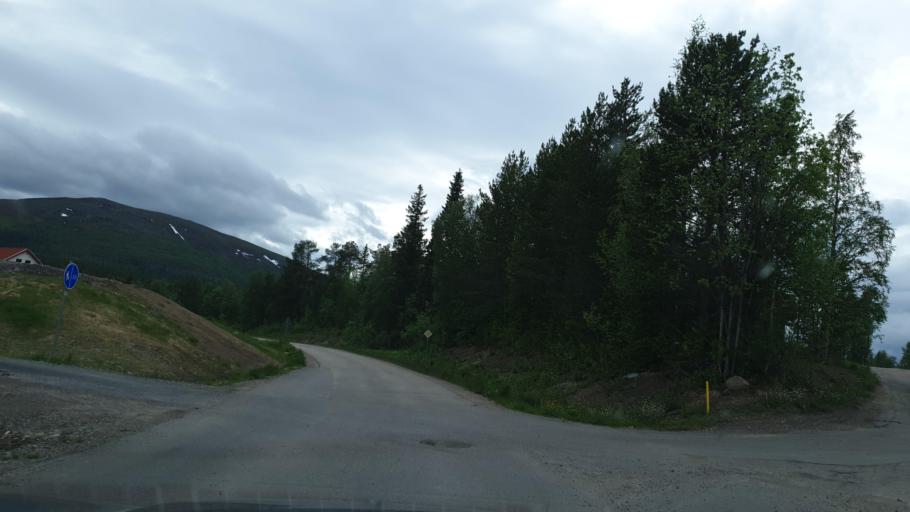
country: SE
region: Norrbotten
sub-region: Gallivare Kommun
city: Gaellivare
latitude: 67.1319
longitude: 20.6291
